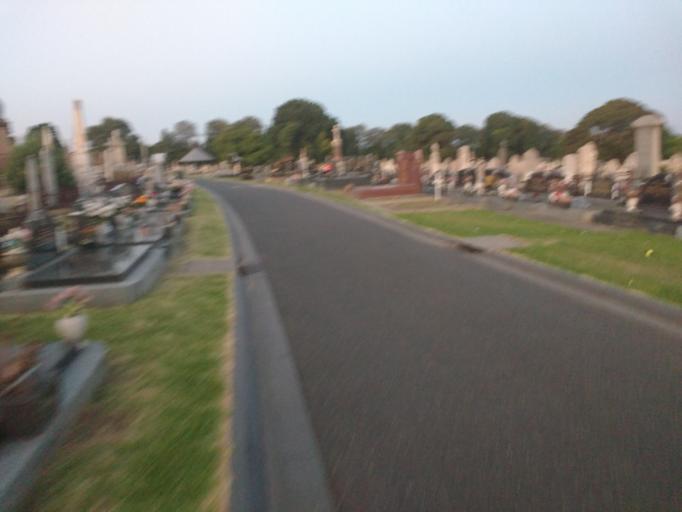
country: AU
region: Victoria
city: Carlton North
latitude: -37.7871
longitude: 144.9658
